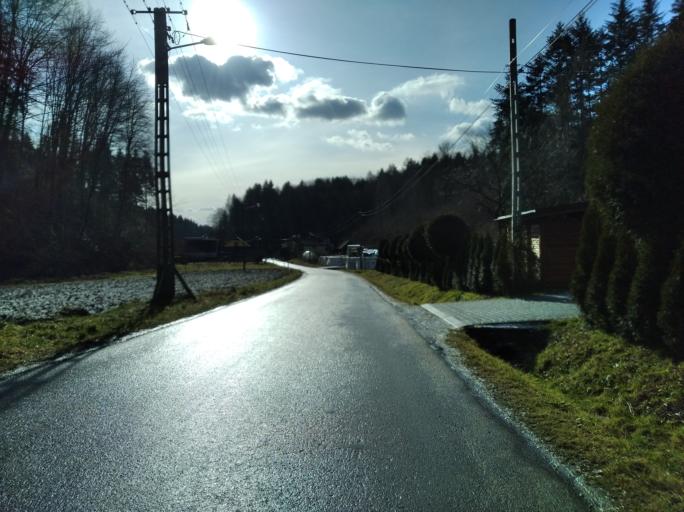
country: PL
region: Subcarpathian Voivodeship
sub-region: Powiat strzyzowski
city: Strzyzow
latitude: 49.8892
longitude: 21.7741
